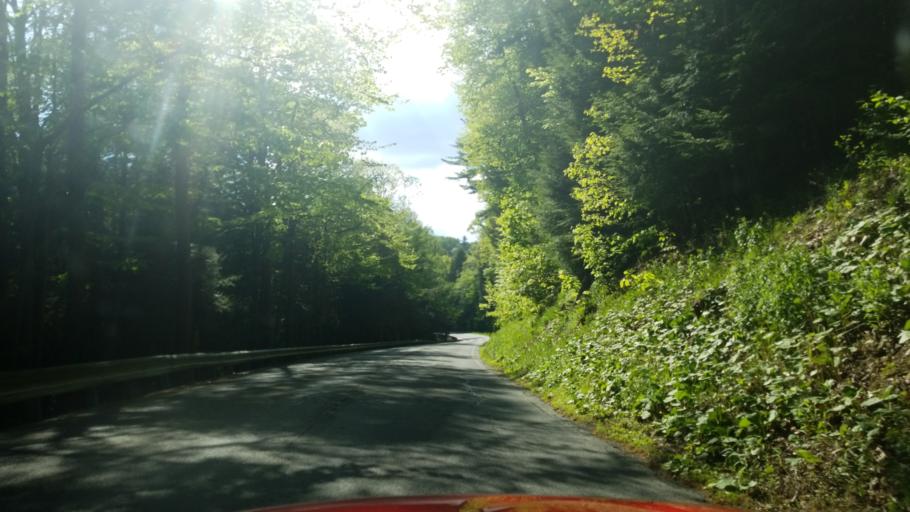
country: US
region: Pennsylvania
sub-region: Clearfield County
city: Hyde
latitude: 40.9715
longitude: -78.4304
